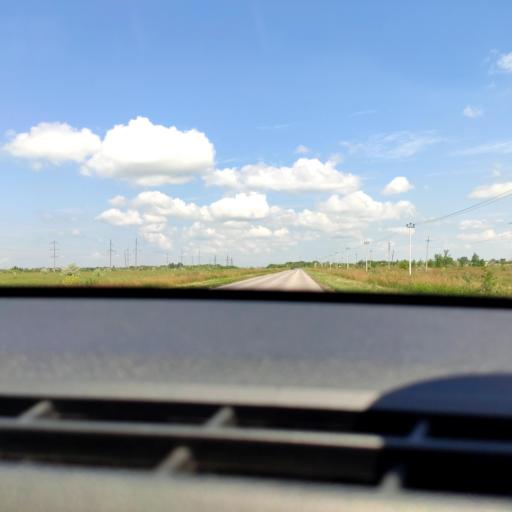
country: RU
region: Samara
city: Podstepki
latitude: 53.5586
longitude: 49.0915
